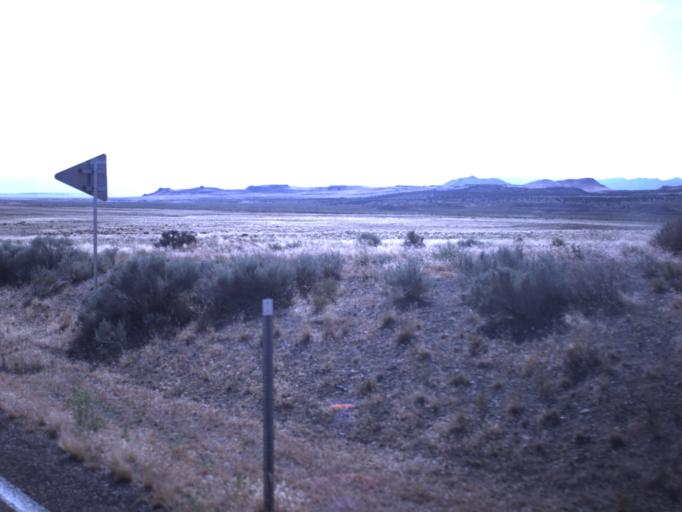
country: US
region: Utah
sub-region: Beaver County
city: Milford
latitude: 38.8097
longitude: -112.8735
